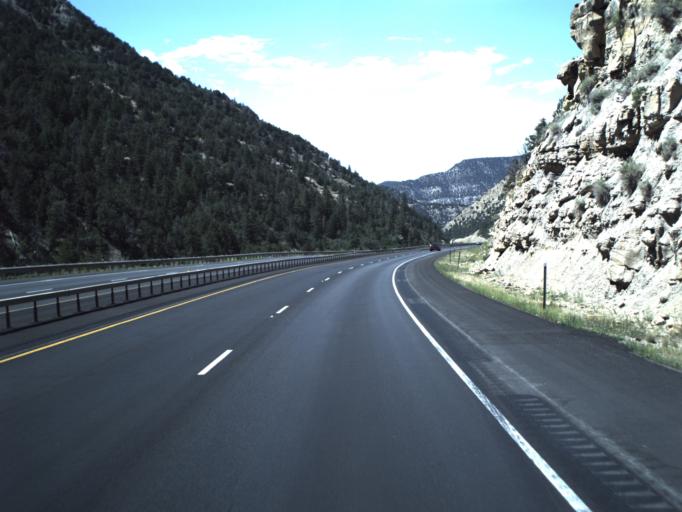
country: US
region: Utah
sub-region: Sevier County
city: Salina
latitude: 38.8866
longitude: -111.6070
